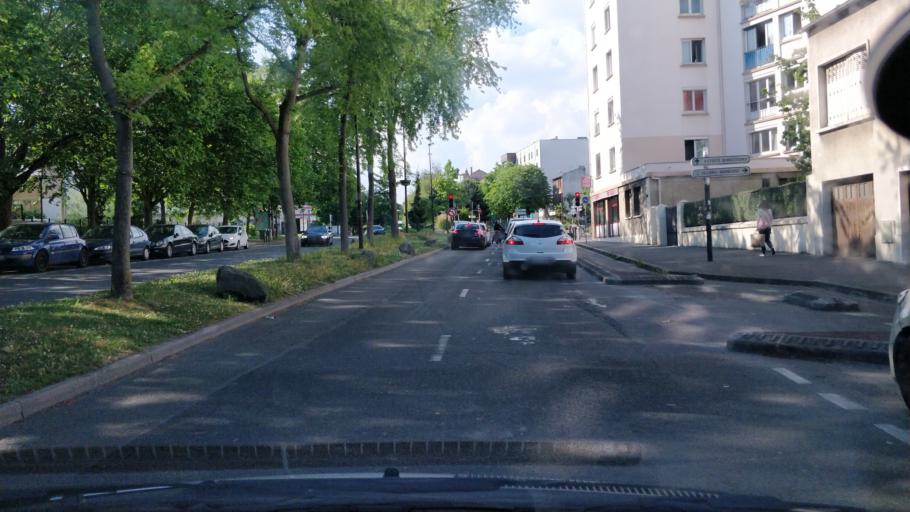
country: FR
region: Ile-de-France
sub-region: Departement de Seine-Saint-Denis
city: Montreuil
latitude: 48.8666
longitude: 2.4348
